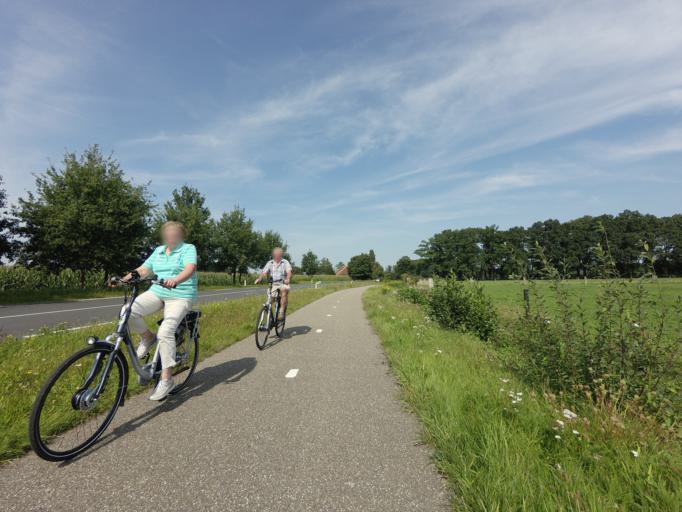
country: NL
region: Overijssel
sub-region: Gemeente Borne
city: Borne
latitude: 52.3289
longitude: 6.7256
